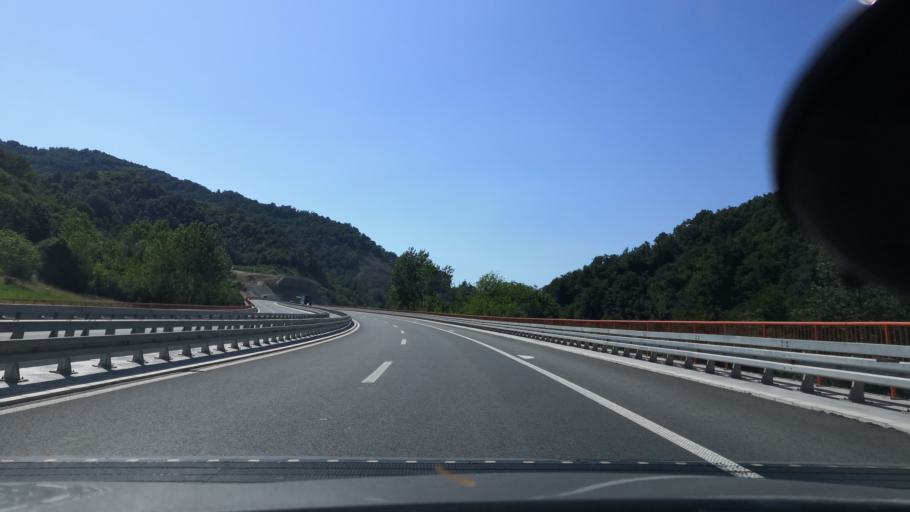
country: RS
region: Central Serbia
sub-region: Jablanicki Okrug
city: Vlasotince
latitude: 42.8640
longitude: 22.1163
